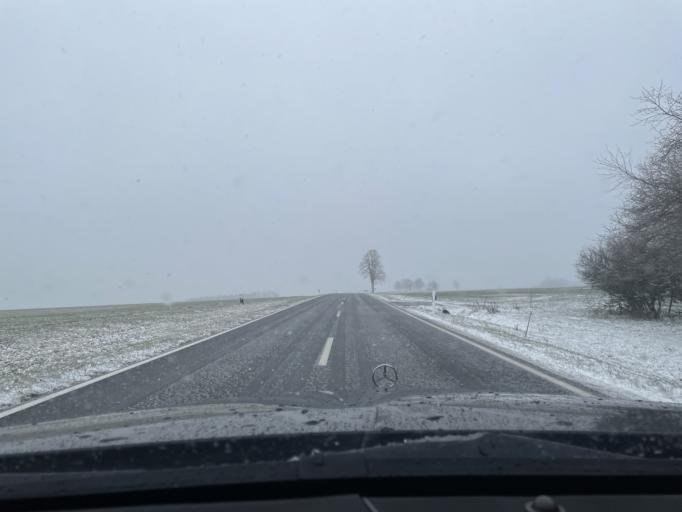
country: DE
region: Thuringia
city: Effelder
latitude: 51.2345
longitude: 10.2688
